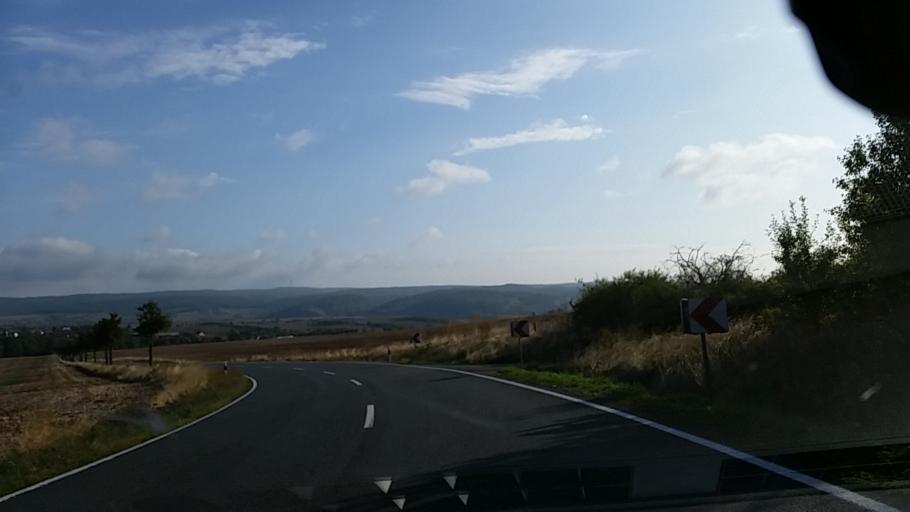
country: DE
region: Thuringia
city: Trebra
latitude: 51.3616
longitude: 10.9941
